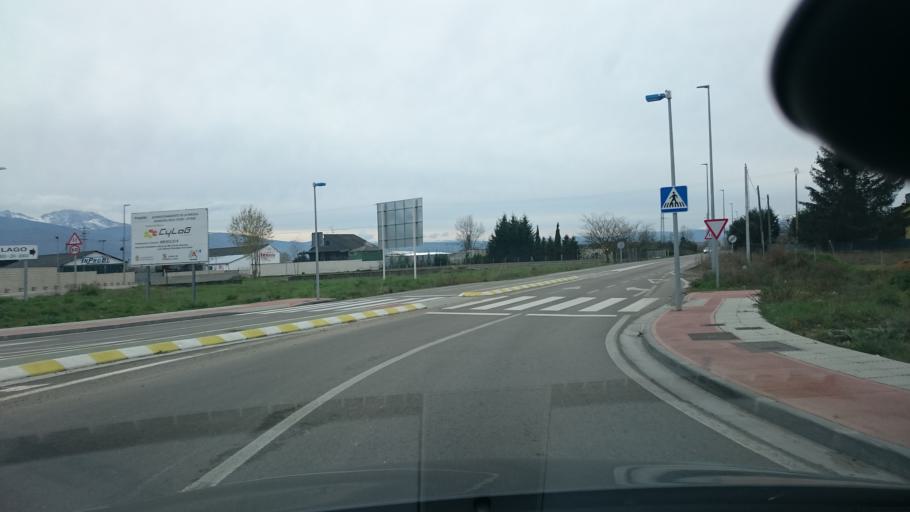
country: ES
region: Castille and Leon
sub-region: Provincia de Leon
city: Camponaraya
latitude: 42.5578
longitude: -6.6357
